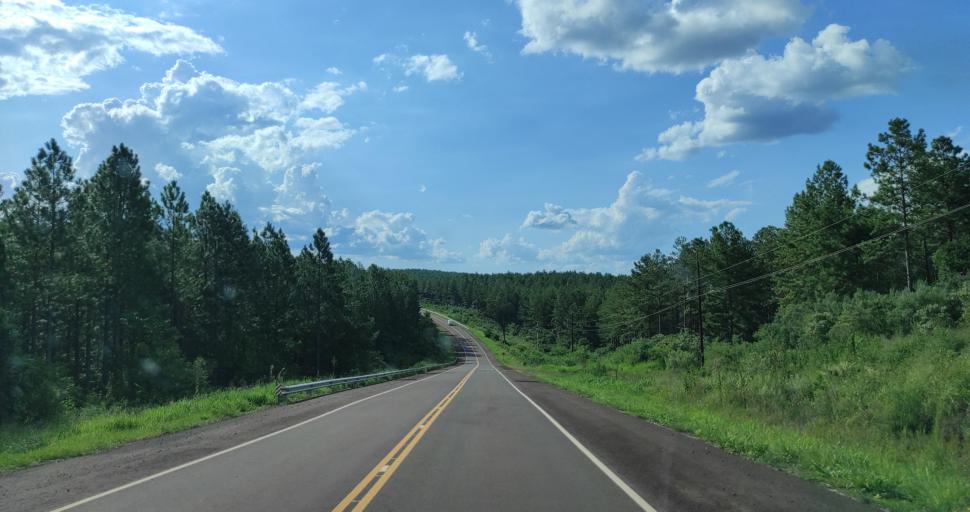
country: AR
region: Misiones
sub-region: Departamento de San Pedro
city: San Pedro
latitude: -26.3557
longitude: -53.9576
